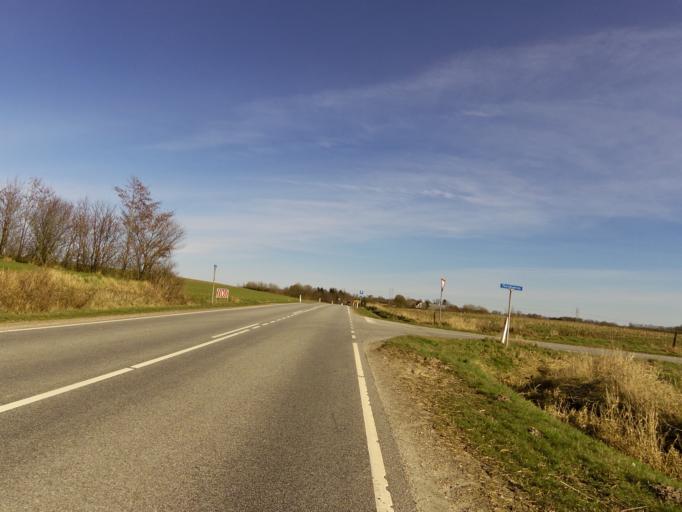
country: DK
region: South Denmark
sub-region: Vejen Kommune
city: Rodding
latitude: 55.3655
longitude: 9.0850
